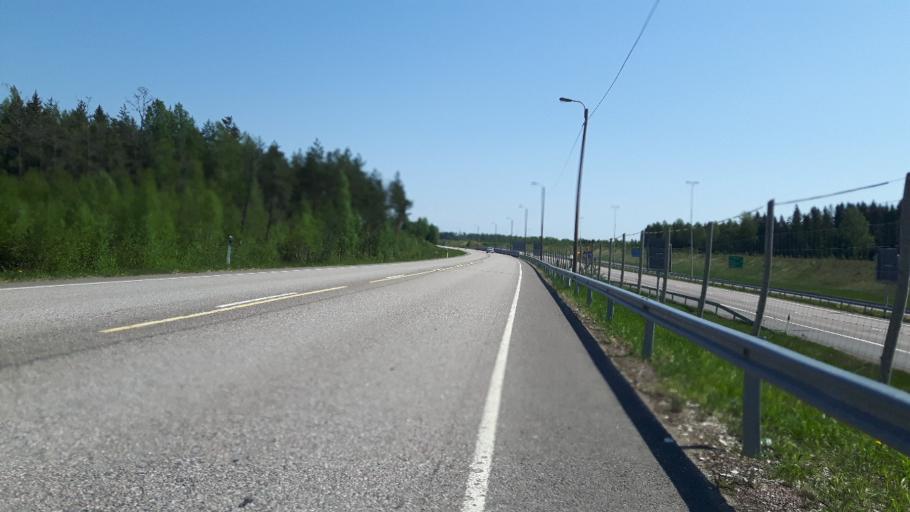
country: FI
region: Uusimaa
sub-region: Loviisa
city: Ruotsinpyhtaeae
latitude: 60.4897
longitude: 26.4640
